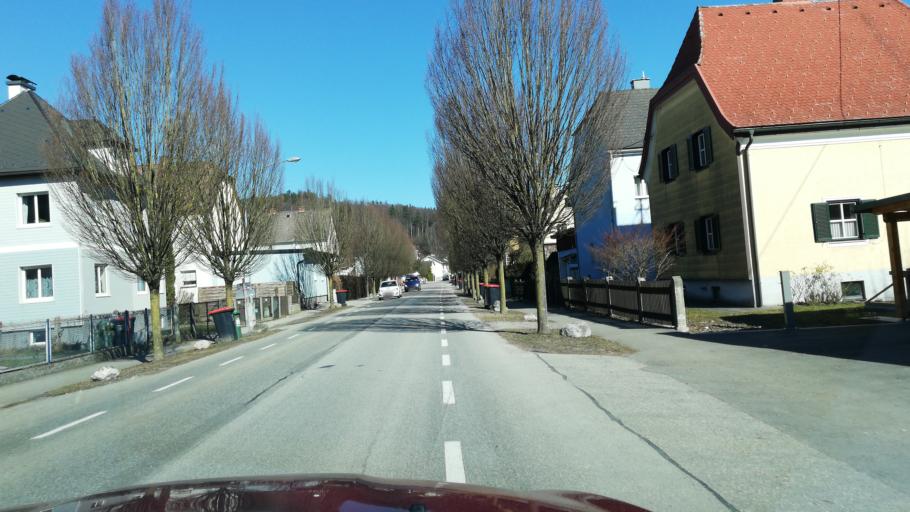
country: AT
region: Upper Austria
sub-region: Politischer Bezirk Vocklabruck
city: Attnang-Puchheim
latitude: 48.0150
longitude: 13.7190
